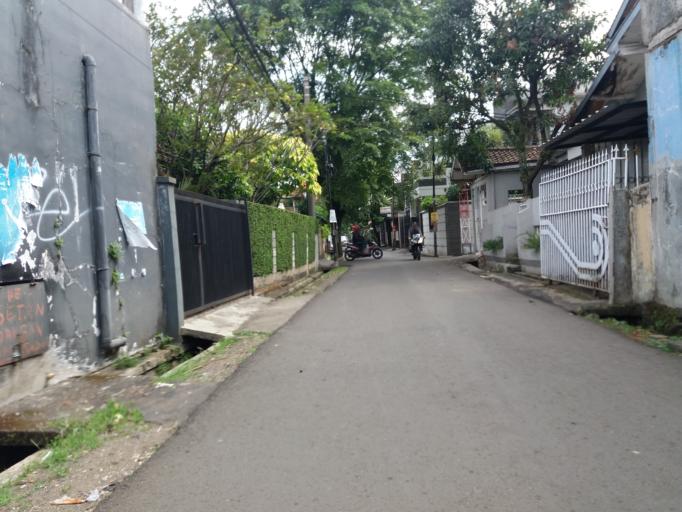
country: ID
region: West Java
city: Bandung
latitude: -6.9198
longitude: 107.6573
